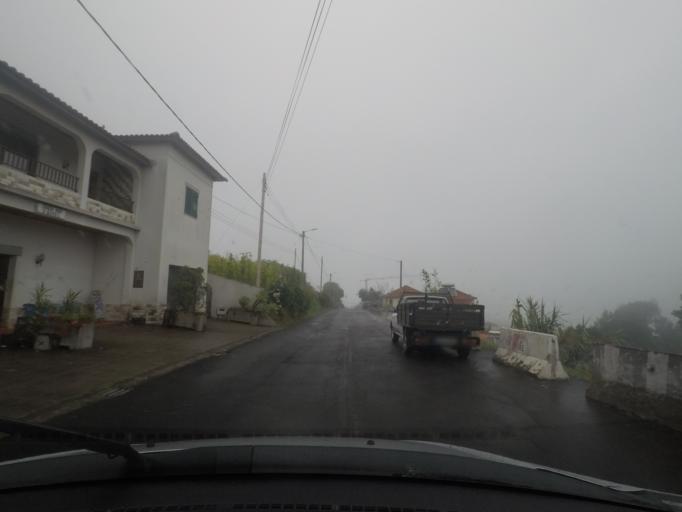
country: PT
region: Madeira
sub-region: Santana
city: Santana
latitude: 32.7982
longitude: -16.8772
